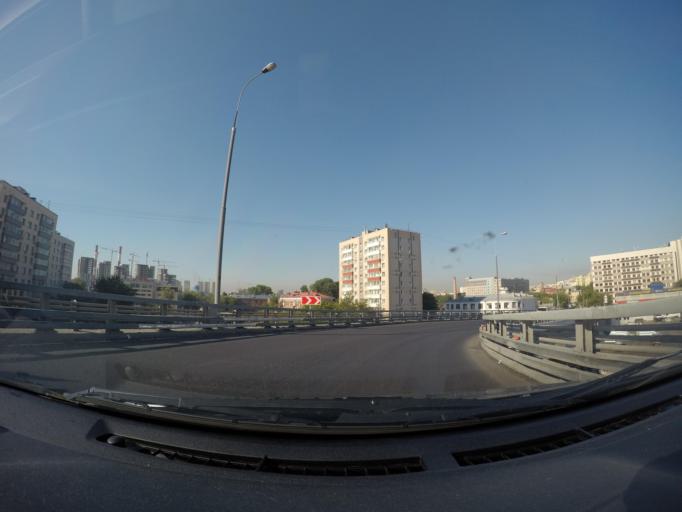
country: RU
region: Moscow
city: Lefortovo
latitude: 55.7360
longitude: 37.6985
